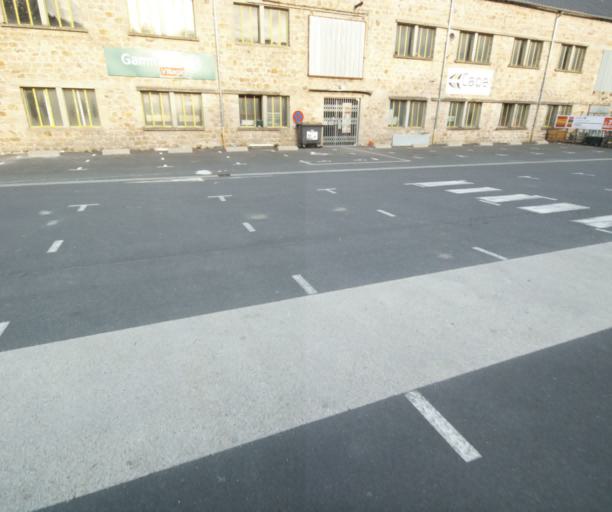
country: FR
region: Limousin
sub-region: Departement de la Correze
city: Correze
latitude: 45.3681
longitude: 1.8718
